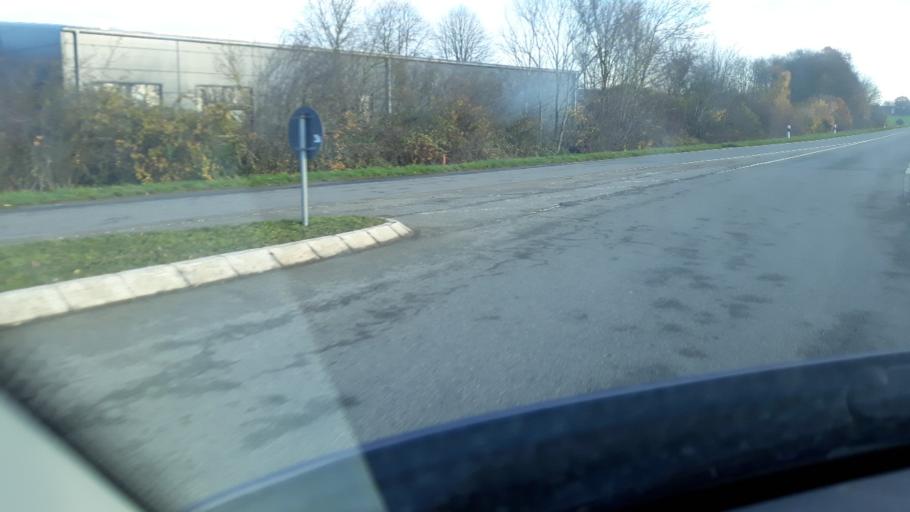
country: DE
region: Schleswig-Holstein
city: Kappeln
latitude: 54.6624
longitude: 9.9510
